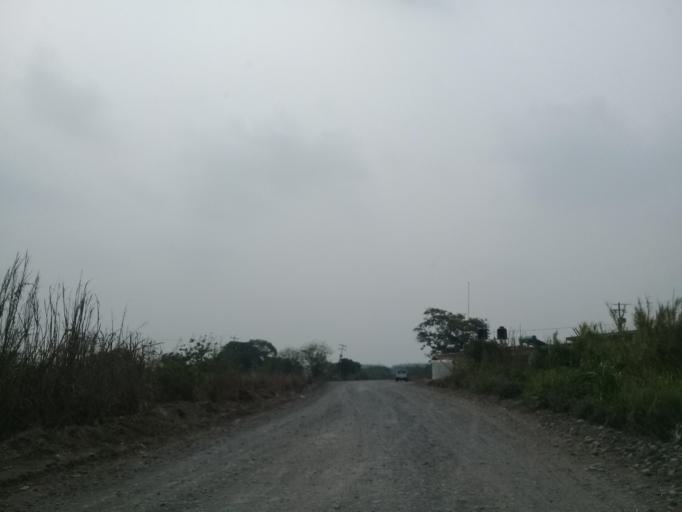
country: MX
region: Veracruz
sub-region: Medellin
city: La Laguna y Monte del Castillo
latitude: 18.9063
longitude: -96.1857
